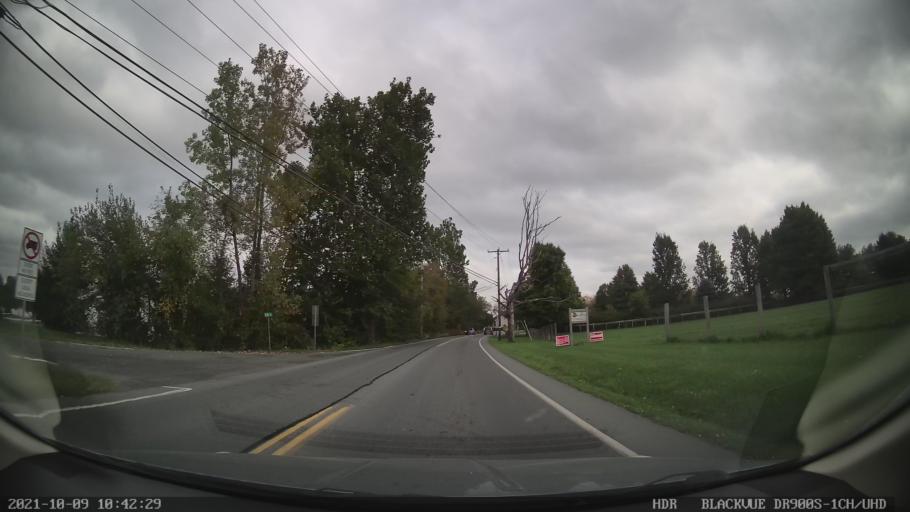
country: US
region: Pennsylvania
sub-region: Lehigh County
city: Trexlertown
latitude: 40.5297
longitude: -75.6088
